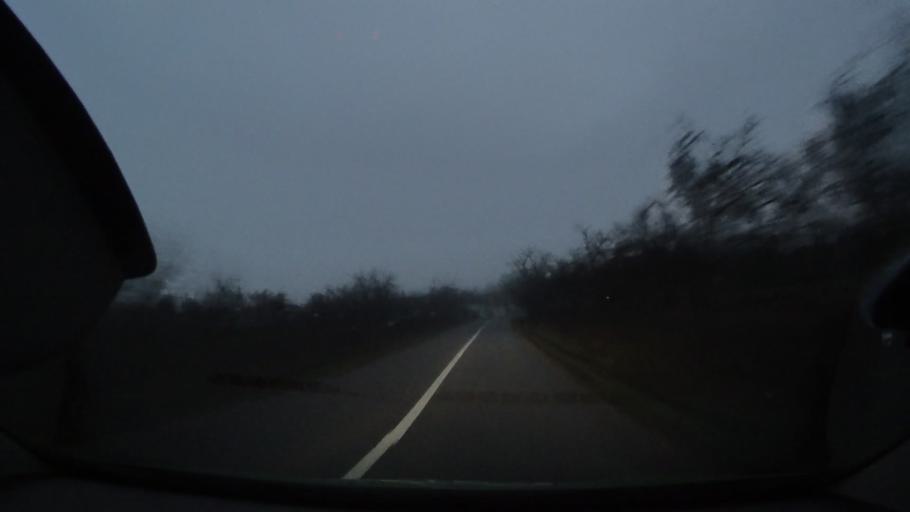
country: RO
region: Arad
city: Hatzmas
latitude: 46.5019
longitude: 22.0778
